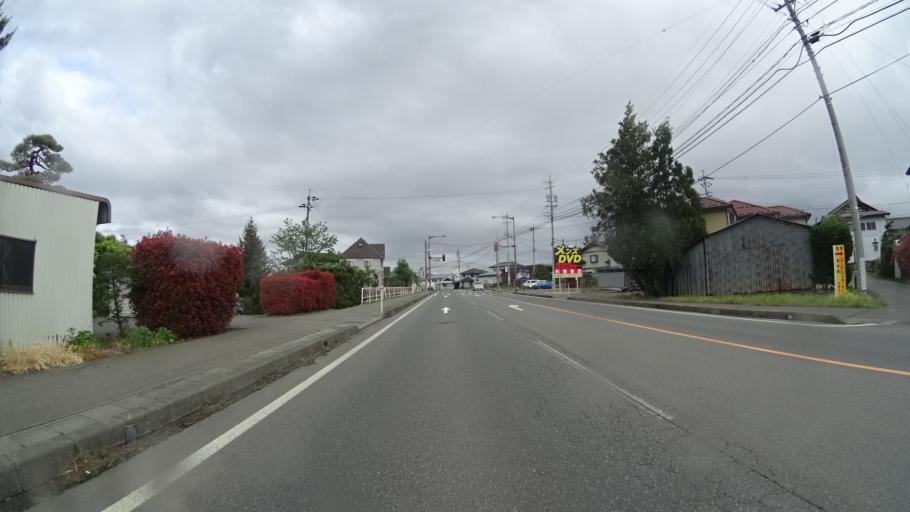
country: JP
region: Nagano
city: Nakano
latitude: 36.7317
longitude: 138.3132
